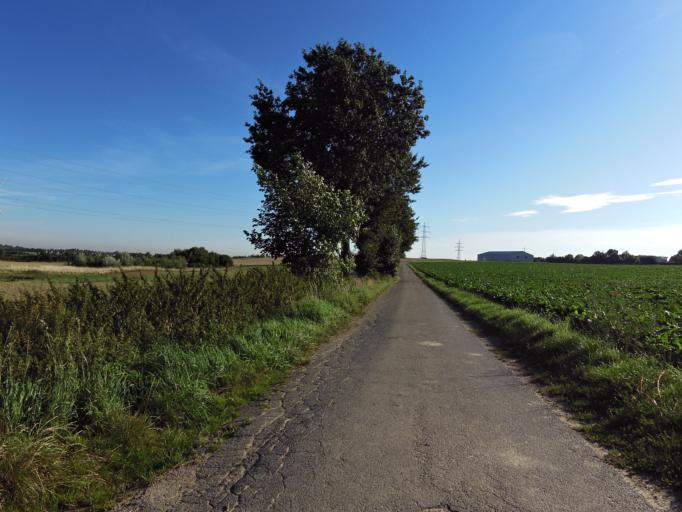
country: DE
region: North Rhine-Westphalia
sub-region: Regierungsbezirk Koln
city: Alsdorf
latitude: 50.8865
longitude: 6.1651
